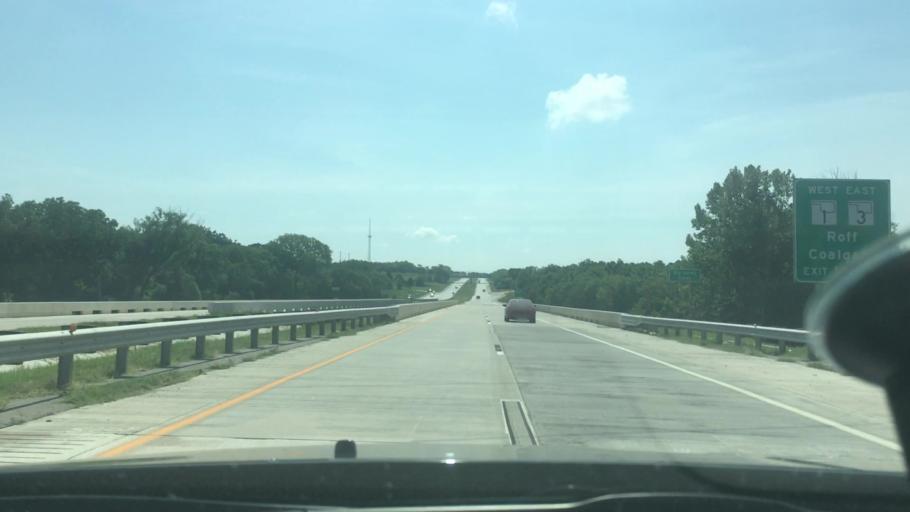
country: US
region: Oklahoma
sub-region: Pontotoc County
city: Ada
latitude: 34.7796
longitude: -96.7109
